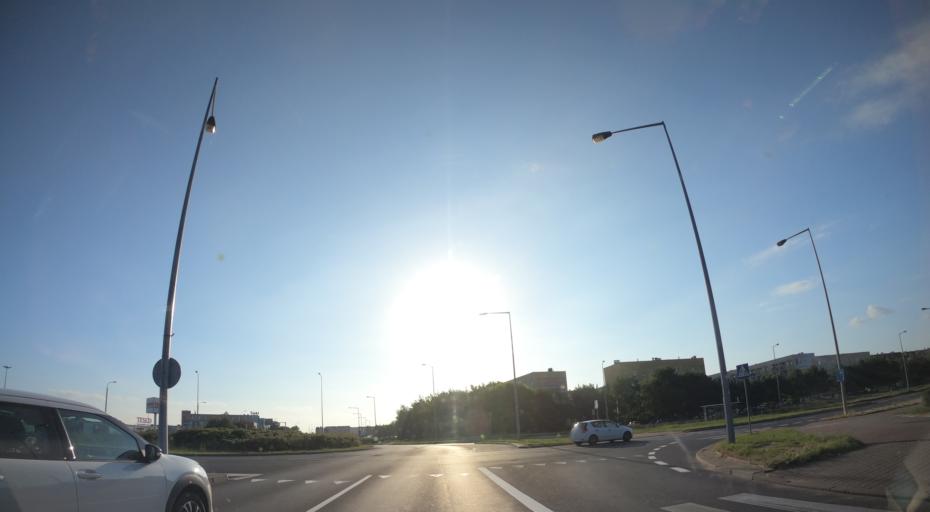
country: PL
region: Lubusz
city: Gorzow Wielkopolski
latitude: 52.7585
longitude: 15.2578
